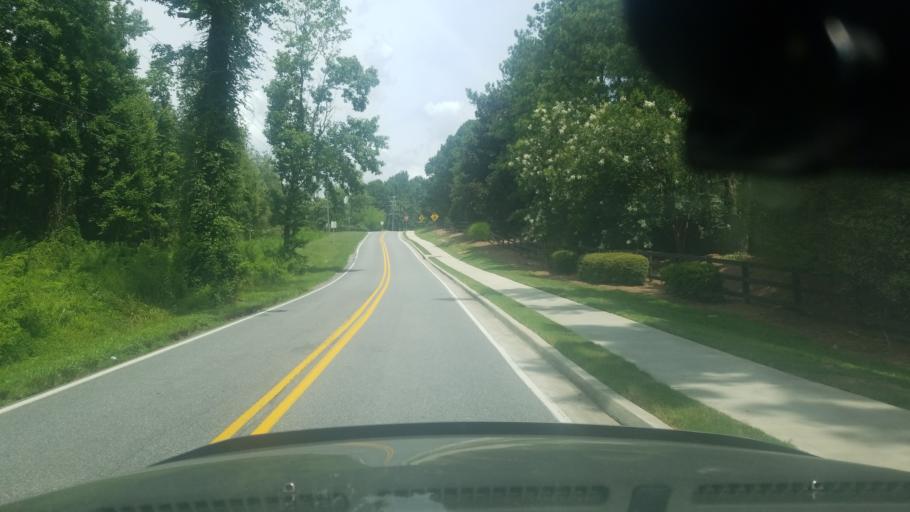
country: US
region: Georgia
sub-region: Fulton County
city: Johns Creek
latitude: 34.1032
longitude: -84.1891
